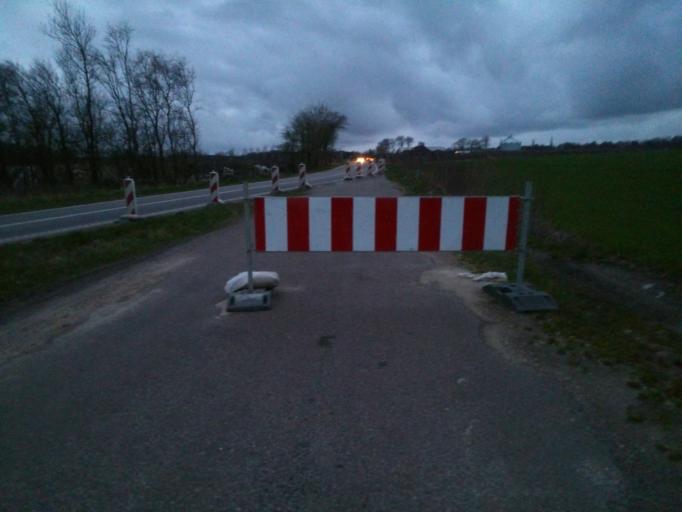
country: DK
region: Central Jutland
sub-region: Herning Kommune
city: Avlum
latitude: 56.3516
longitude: 8.7389
